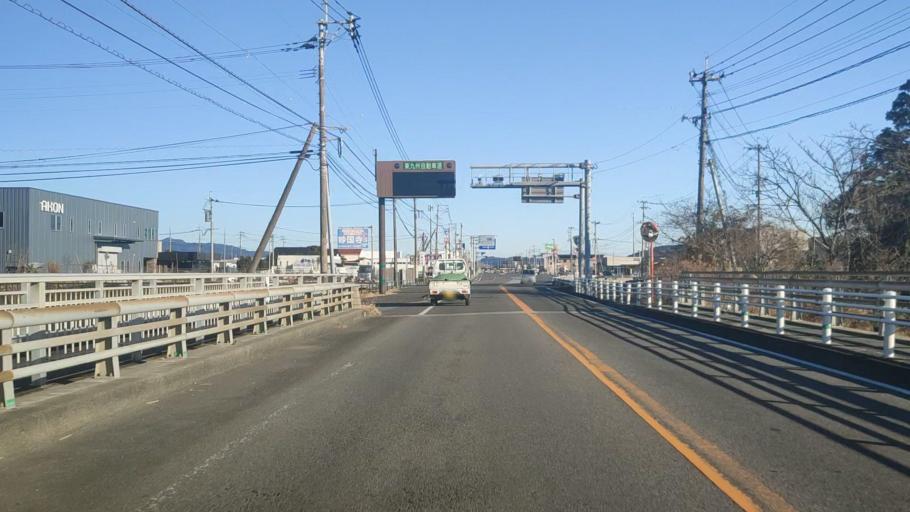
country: JP
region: Miyazaki
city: Nobeoka
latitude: 32.3947
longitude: 131.6288
